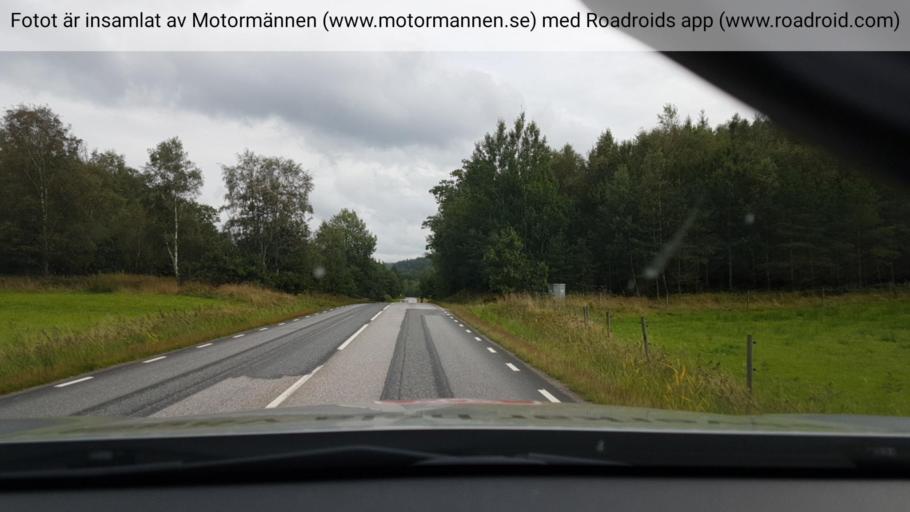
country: SE
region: Vaestra Goetaland
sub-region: Sotenas Kommun
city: Hunnebostrand
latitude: 58.5526
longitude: 11.4081
